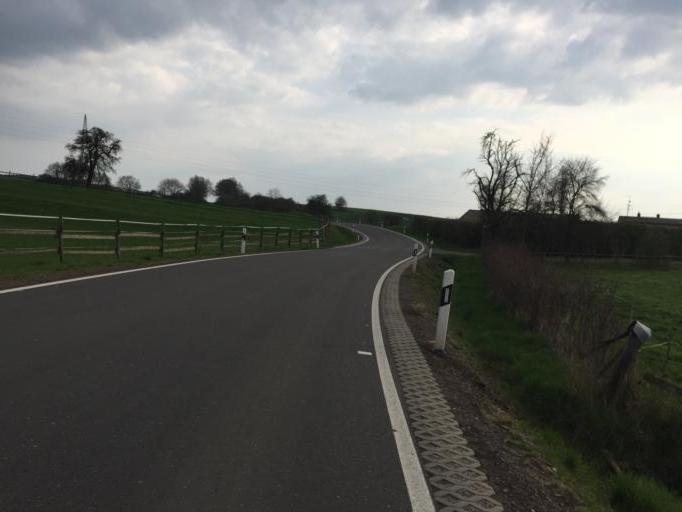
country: DE
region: Hesse
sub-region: Regierungsbezirk Giessen
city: Grunberg
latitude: 50.5807
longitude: 8.9669
